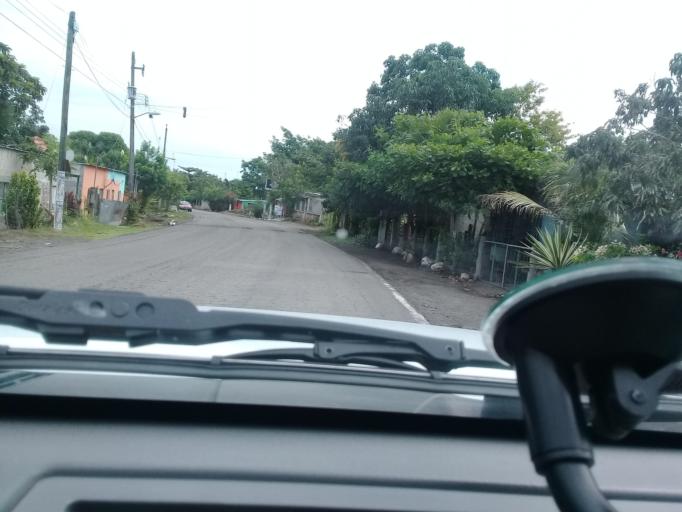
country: MX
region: Veracruz
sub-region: Paso de Ovejas
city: El Hatito
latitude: 19.3121
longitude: -96.3829
